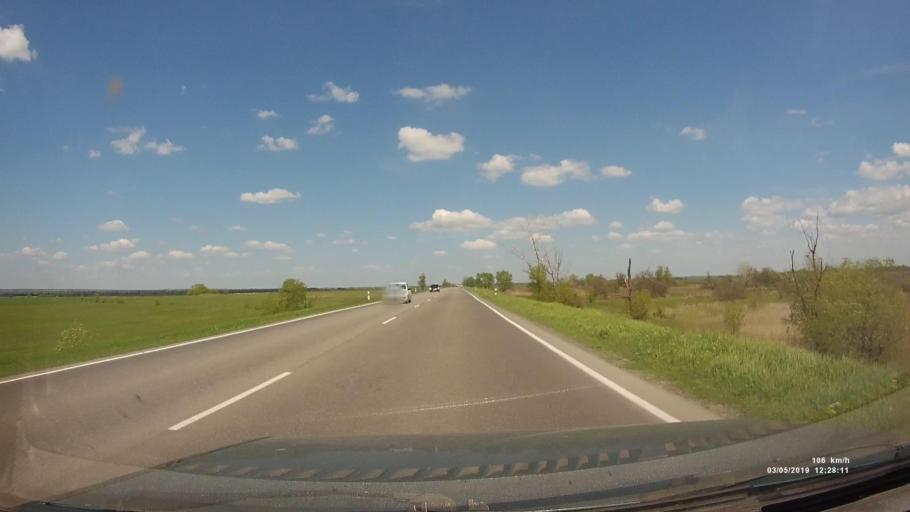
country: RU
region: Rostov
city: Semikarakorsk
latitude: 47.4698
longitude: 40.7264
